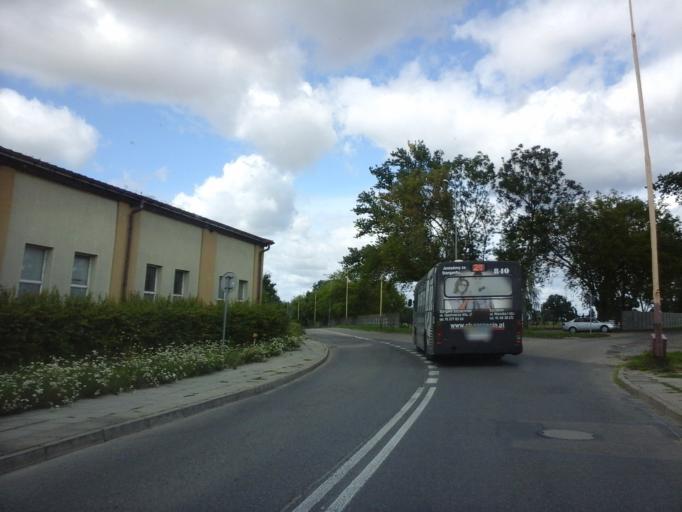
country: PL
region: West Pomeranian Voivodeship
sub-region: Powiat pyrzycki
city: Warnice
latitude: 53.3005
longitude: 15.0045
